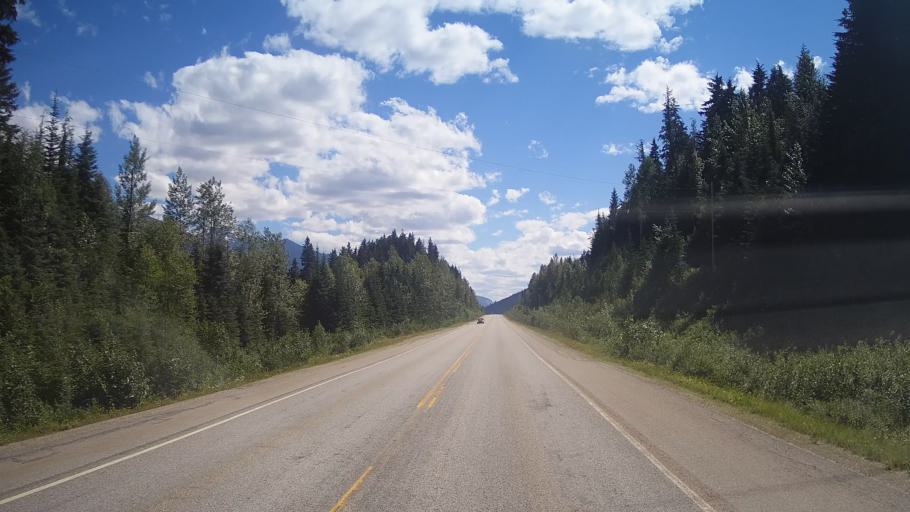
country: CA
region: Alberta
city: Jasper Park Lodge
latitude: 52.5539
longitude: -119.1117
